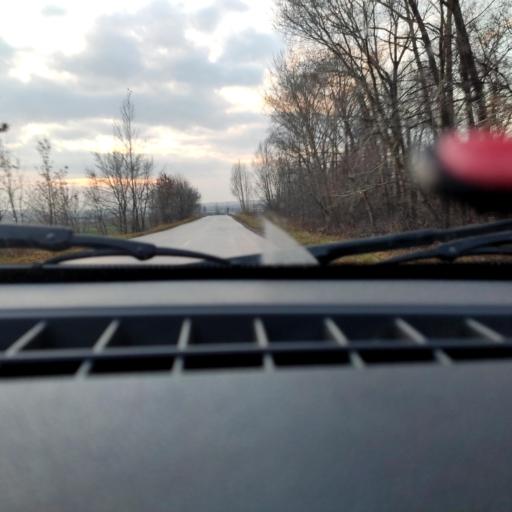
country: RU
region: Bashkortostan
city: Avdon
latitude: 54.5096
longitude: 55.8296
